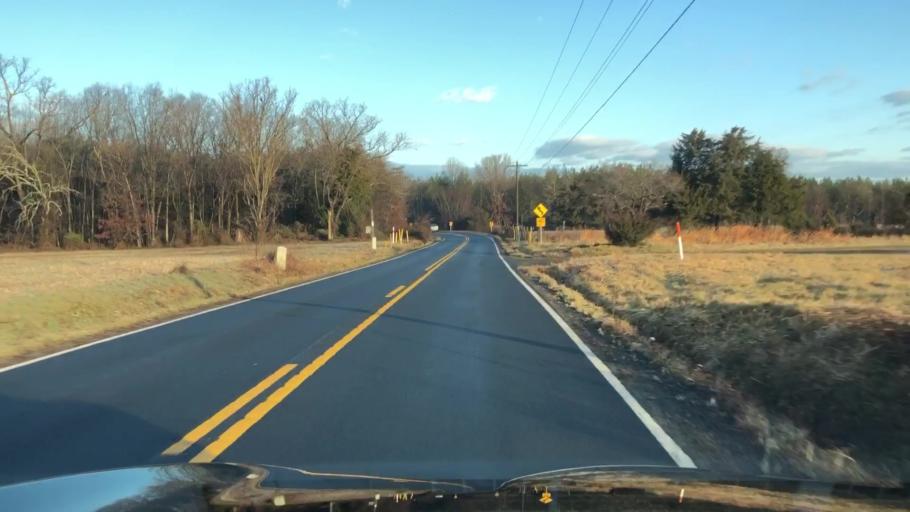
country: US
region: Virginia
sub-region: Fauquier County
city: Bealeton
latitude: 38.5855
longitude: -77.6996
